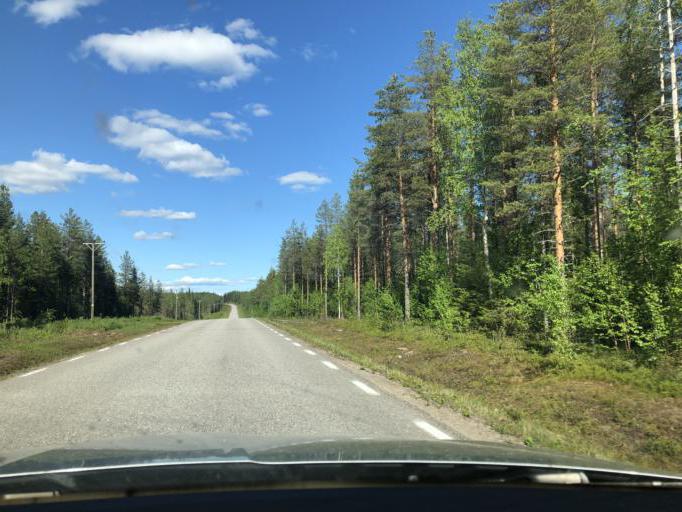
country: SE
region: Norrbotten
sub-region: Kalix Kommun
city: Kalix
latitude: 66.0930
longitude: 23.2521
